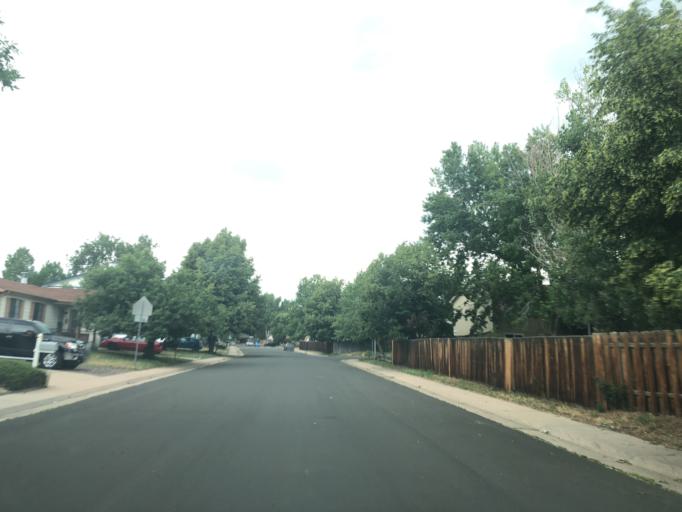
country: US
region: Colorado
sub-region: Arapahoe County
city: Dove Valley
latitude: 39.6269
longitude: -104.7813
